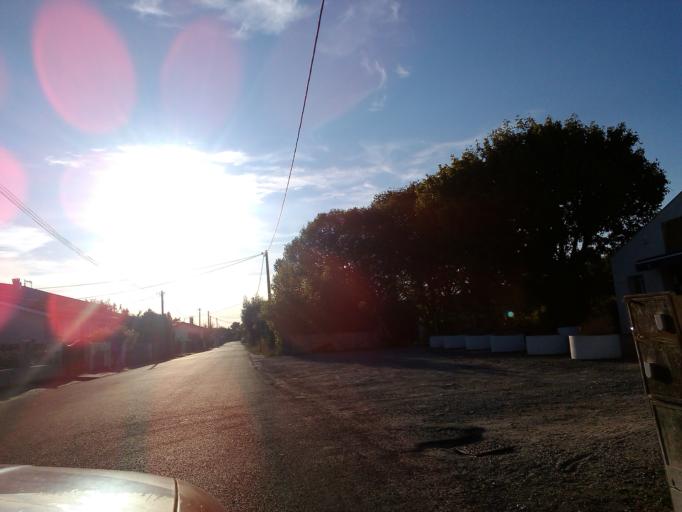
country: FR
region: Aquitaine
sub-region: Departement de la Gironde
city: Soulac-sur-Mer
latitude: 45.4314
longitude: -1.0362
